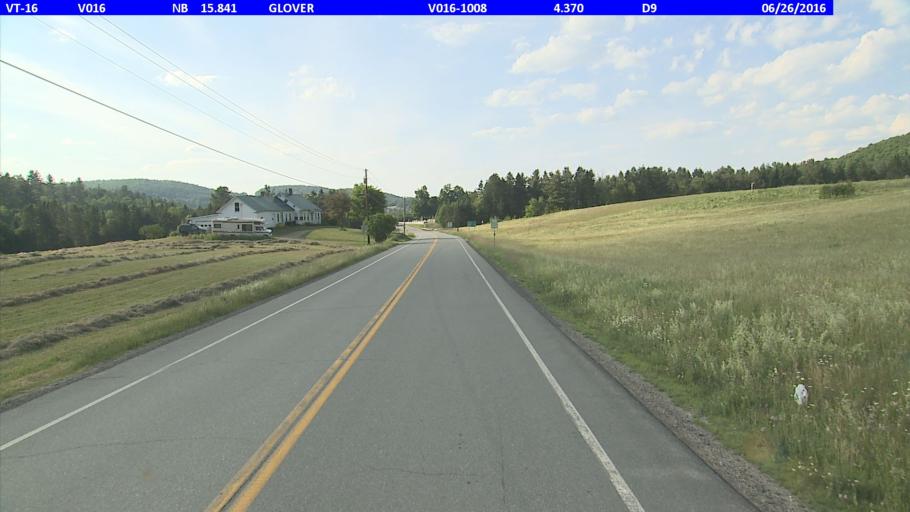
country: US
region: Vermont
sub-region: Caledonia County
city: Lyndonville
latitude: 44.6850
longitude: -72.1905
